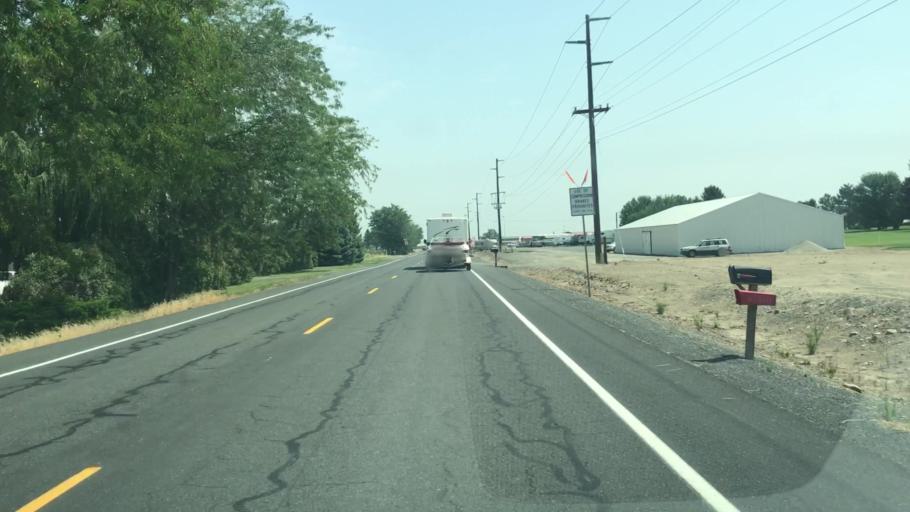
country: US
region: Washington
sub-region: Grant County
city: Quincy
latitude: 47.1613
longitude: -119.8586
